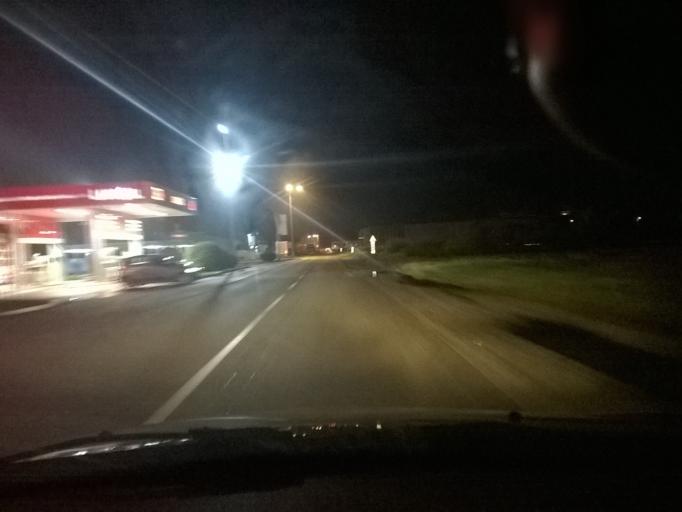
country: HR
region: Krapinsko-Zagorska
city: Zabok
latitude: 46.0172
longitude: 15.8921
